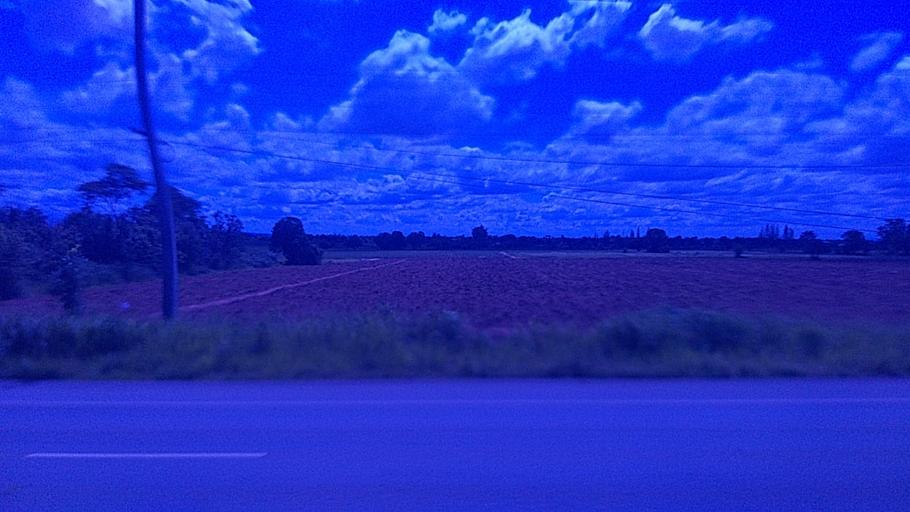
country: TH
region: Nakhon Ratchasima
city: Dan Khun Thot
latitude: 15.0768
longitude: 101.7141
